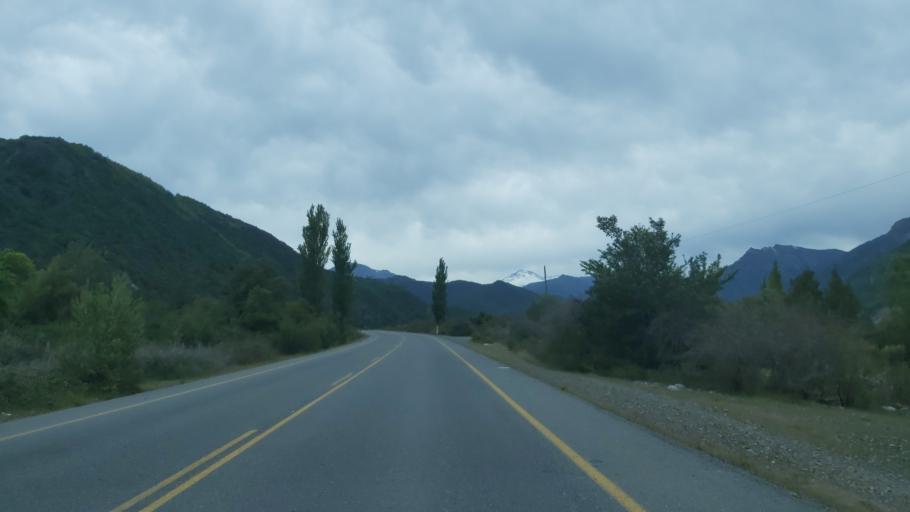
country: CL
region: Maule
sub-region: Provincia de Linares
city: Colbun
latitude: -35.7313
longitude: -71.0146
